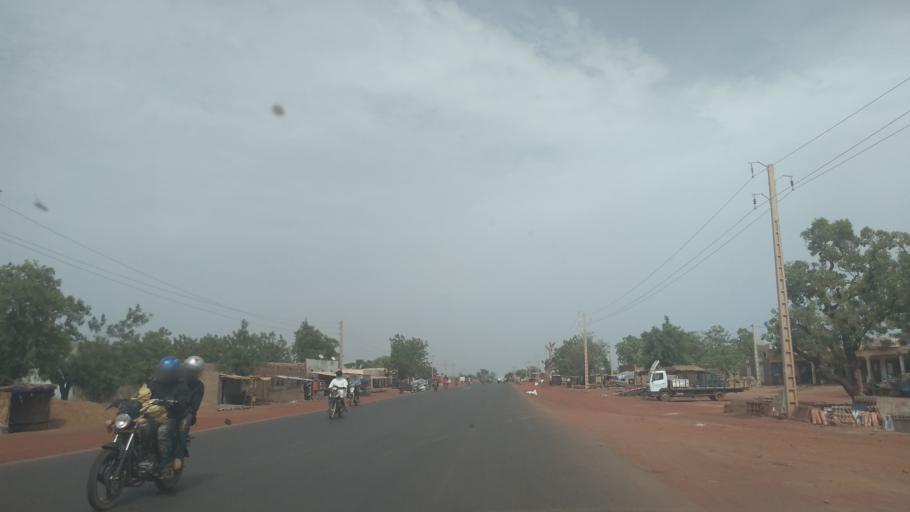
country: ML
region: Bamako
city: Bamako
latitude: 12.5853
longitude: -7.8267
